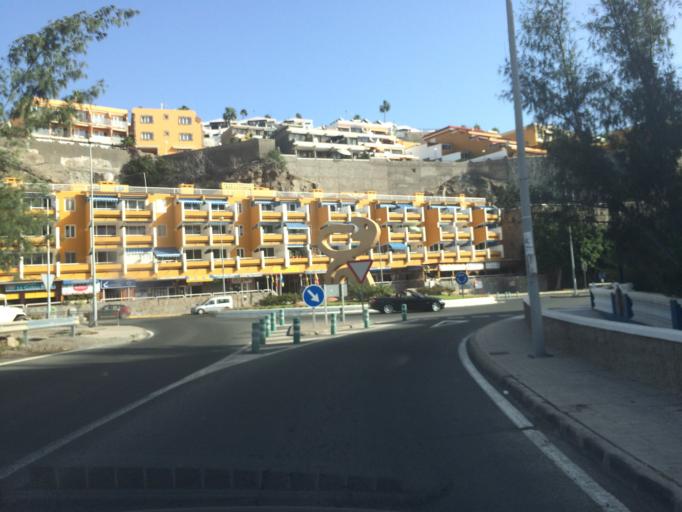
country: ES
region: Canary Islands
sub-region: Provincia de Las Palmas
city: Puerto Rico
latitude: 27.7711
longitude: -15.6879
